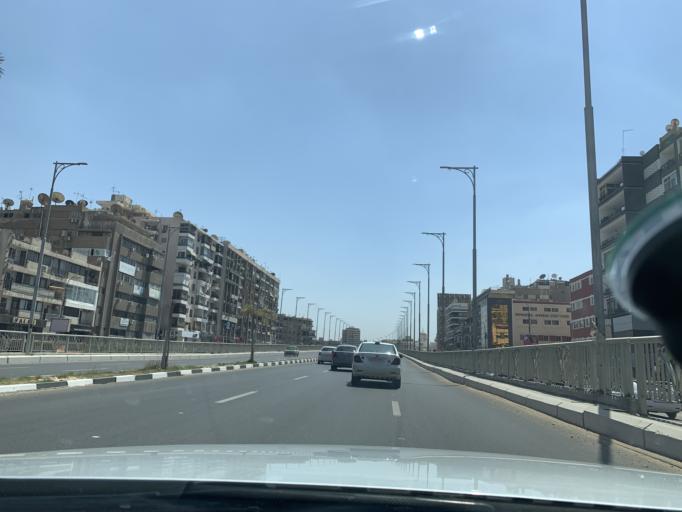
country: EG
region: Muhafazat al Qahirah
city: Cairo
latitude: 30.0887
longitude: 31.3376
